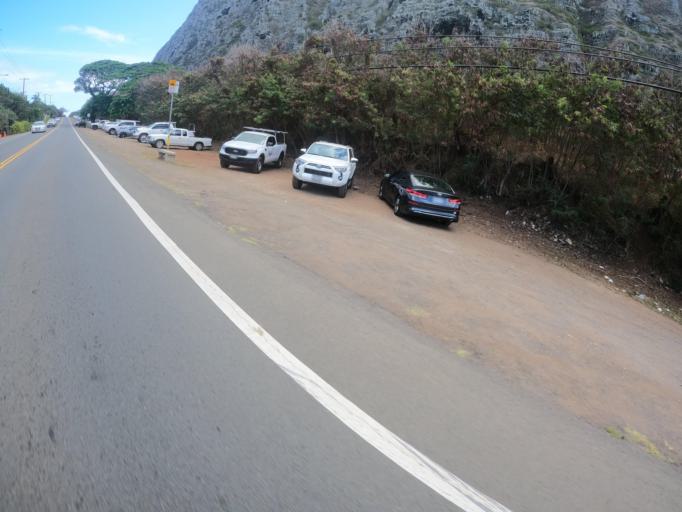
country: US
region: Hawaii
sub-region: Honolulu County
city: Waimanalo Beach
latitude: 21.3248
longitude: -157.6813
